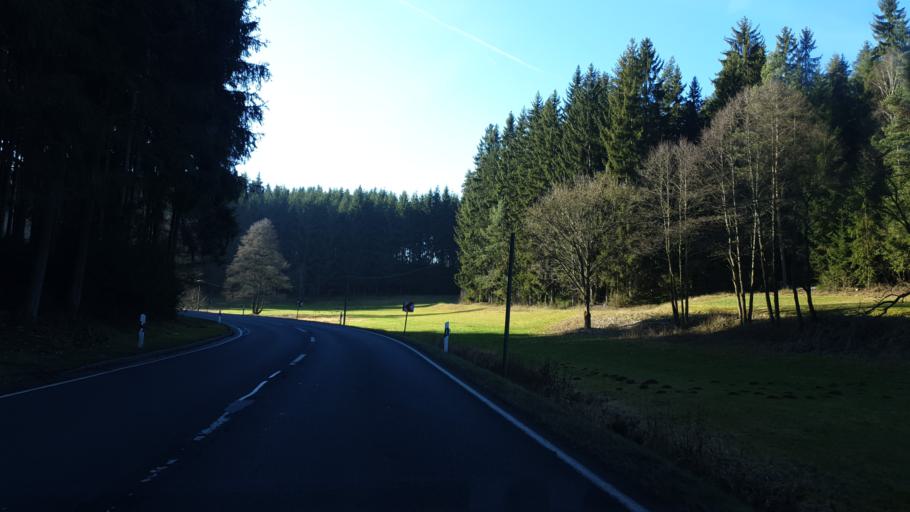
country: DE
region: Saxony
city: Bad Brambach
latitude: 50.2529
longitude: 12.3027
